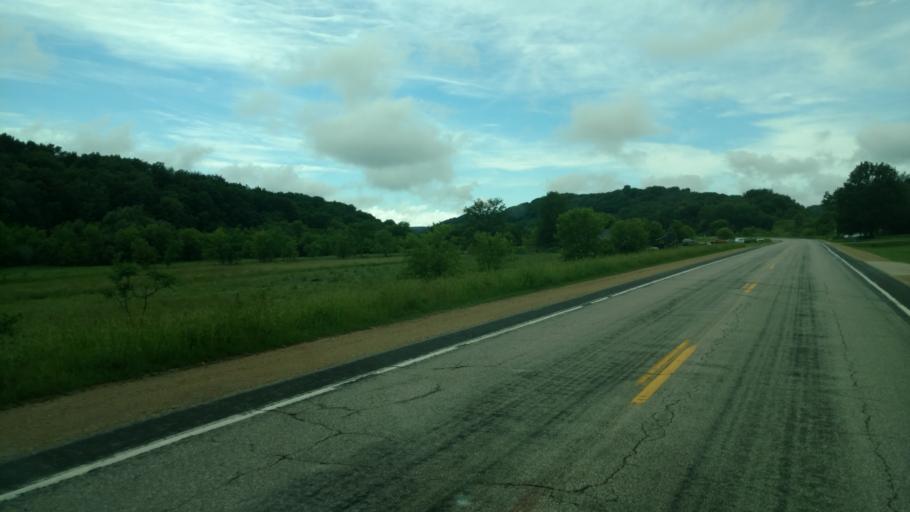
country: US
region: Wisconsin
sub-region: Vernon County
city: Hillsboro
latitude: 43.6579
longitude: -90.3970
